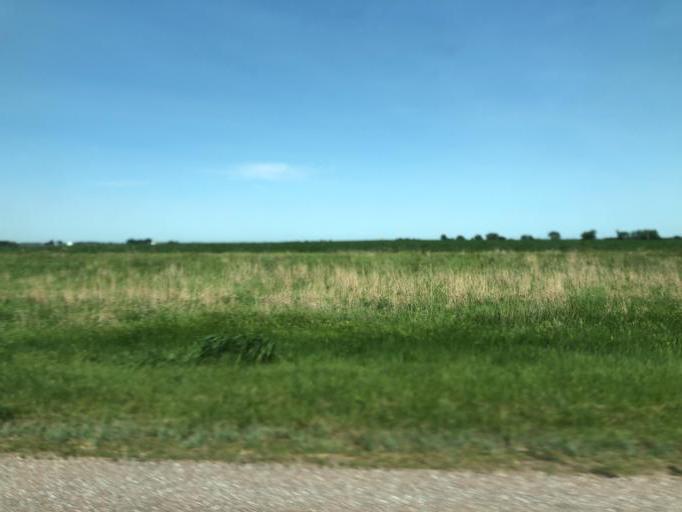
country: US
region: Nebraska
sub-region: York County
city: York
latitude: 40.8008
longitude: -97.5974
